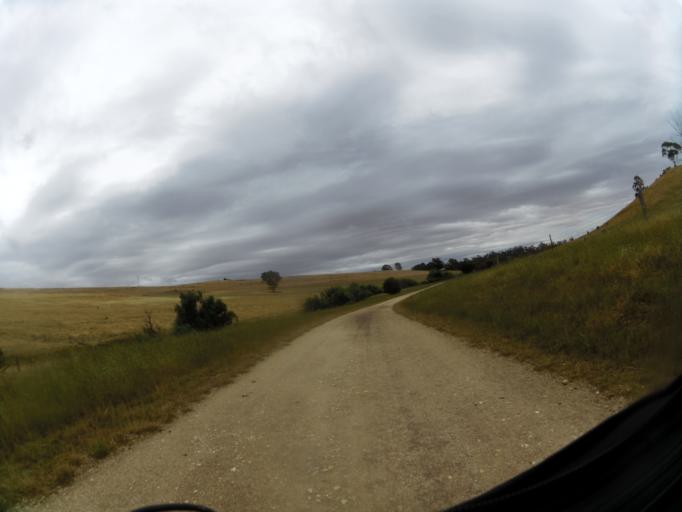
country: AU
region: Victoria
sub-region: Mount Alexander
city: Castlemaine
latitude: -37.2036
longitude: 144.0186
